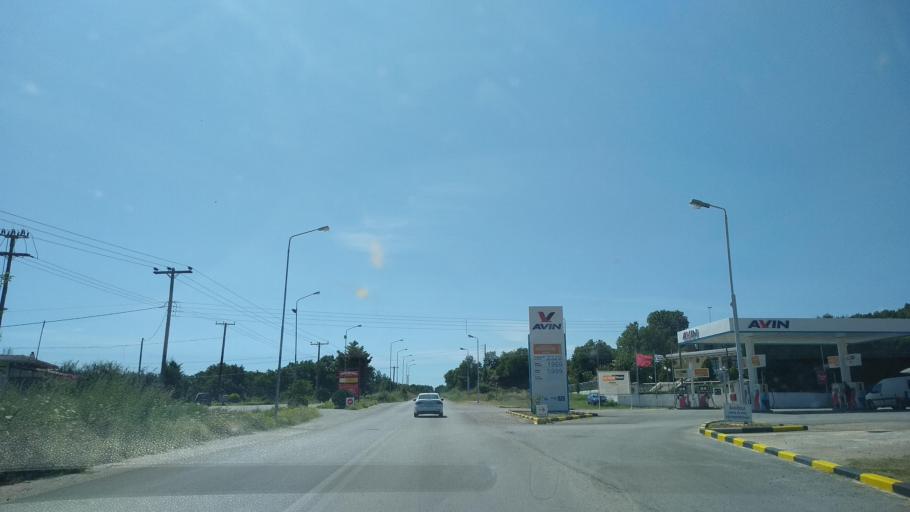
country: GR
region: Central Macedonia
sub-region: Nomos Chalkidikis
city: Megali Panagia
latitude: 40.4189
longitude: 23.6901
